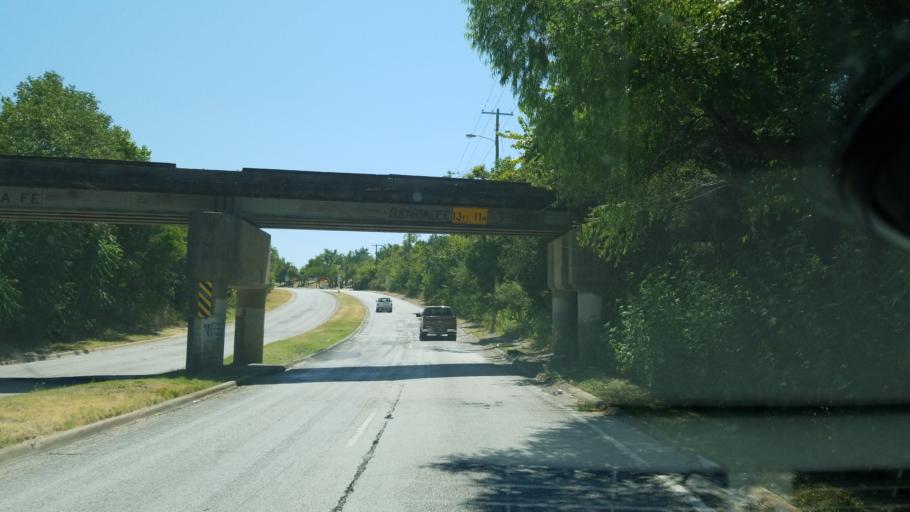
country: US
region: Texas
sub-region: Dallas County
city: Cockrell Hill
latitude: 32.7376
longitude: -96.8980
